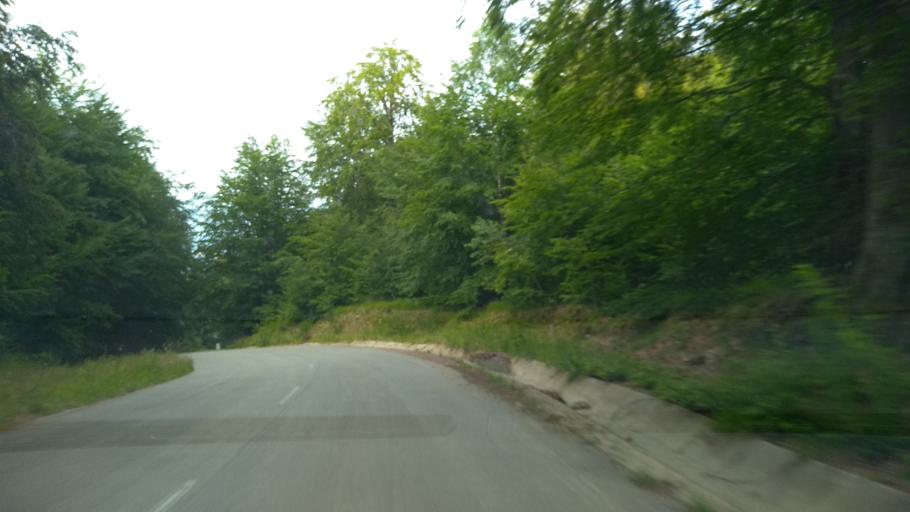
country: RO
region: Hunedoara
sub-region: Municipiul  Vulcan
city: Jiu-Paroseni
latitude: 45.3312
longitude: 23.2886
